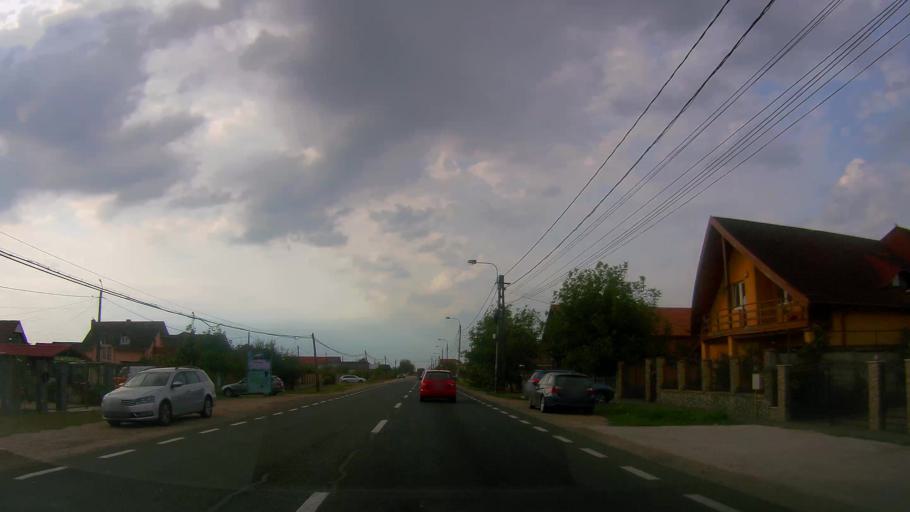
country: RO
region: Satu Mare
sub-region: Oras Ardud
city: Madaras
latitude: 47.7351
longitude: 22.8825
